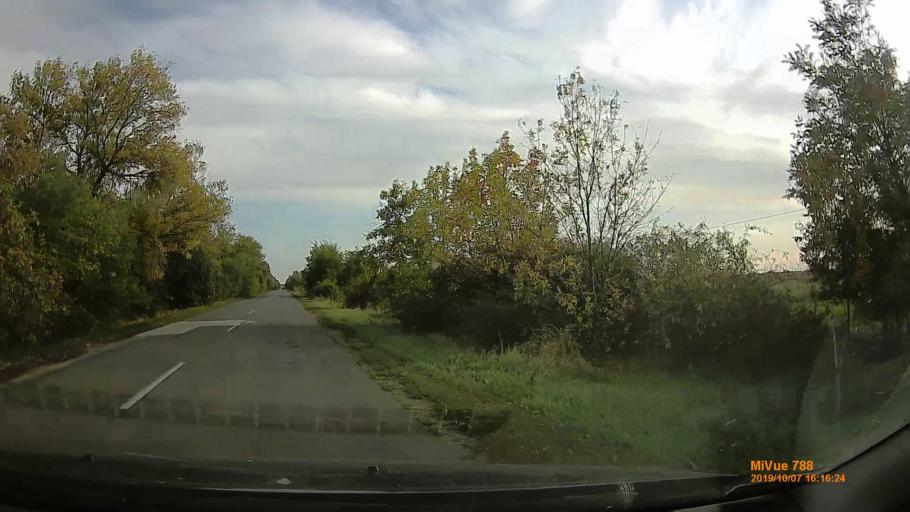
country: HU
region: Bekes
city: Szarvas
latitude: 46.8055
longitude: 20.6185
